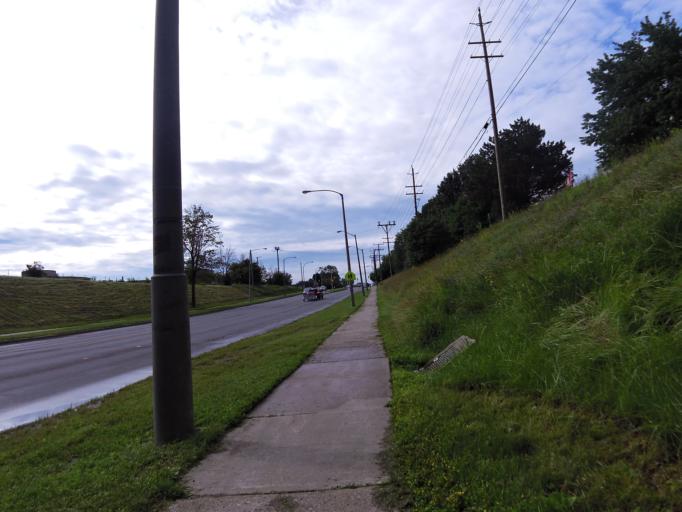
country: CA
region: Ontario
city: Bells Corners
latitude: 45.3339
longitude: -75.7841
